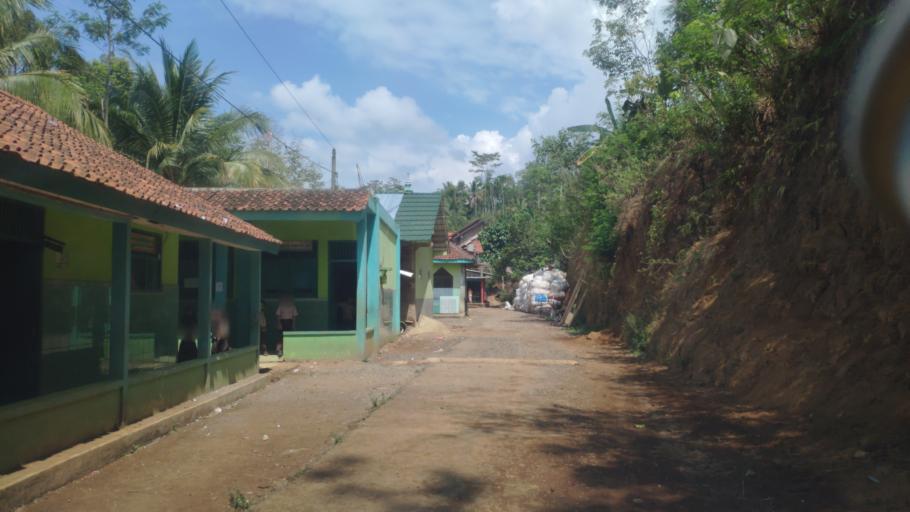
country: ID
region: Central Java
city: Purbalingga
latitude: -7.3443
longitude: 109.6115
